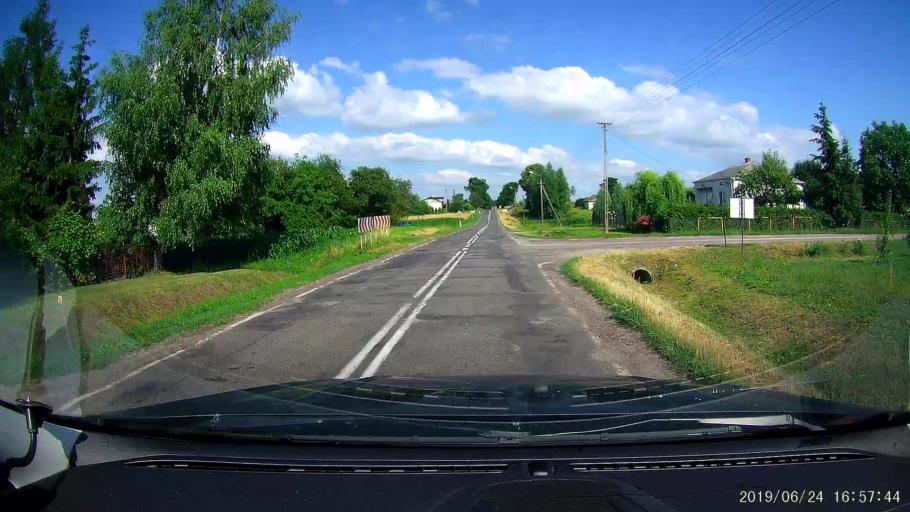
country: PL
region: Lublin Voivodeship
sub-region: Powiat tomaszowski
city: Telatyn
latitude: 50.5260
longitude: 23.8647
